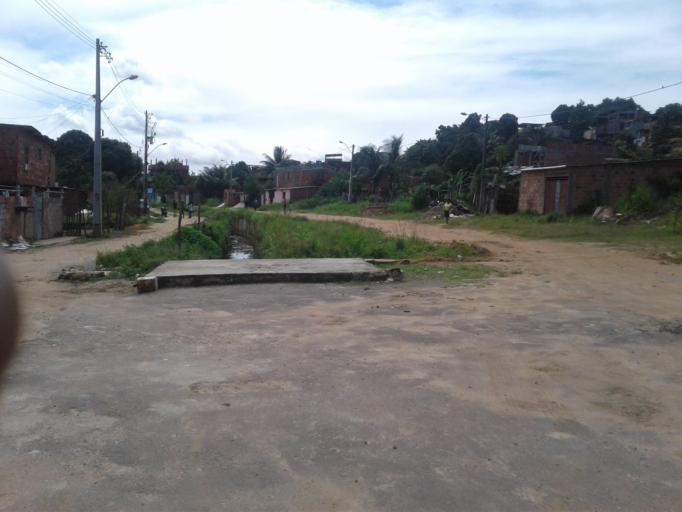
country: BR
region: Bahia
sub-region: Salvador
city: Salvador
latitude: -12.8830
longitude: -38.4749
